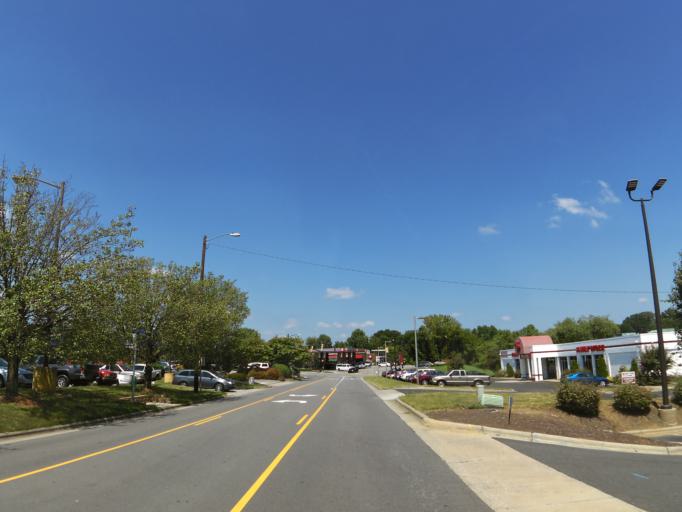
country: US
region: North Carolina
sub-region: Cabarrus County
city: Kannapolis
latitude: 35.4495
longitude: -80.6086
